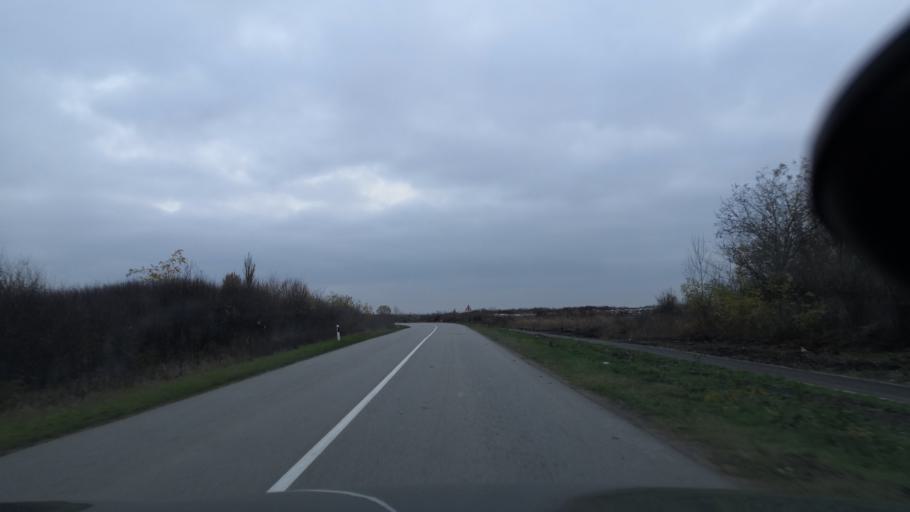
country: RS
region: Autonomna Pokrajina Vojvodina
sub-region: Severnobanatski Okrug
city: Novi Knezevac
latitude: 46.0775
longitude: 20.1037
